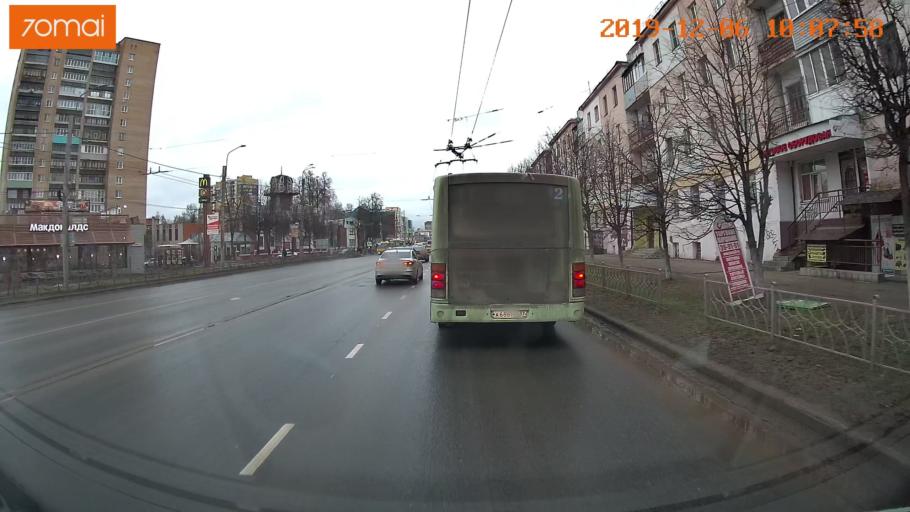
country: RU
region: Ivanovo
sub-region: Gorod Ivanovo
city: Ivanovo
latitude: 57.0150
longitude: 40.9703
